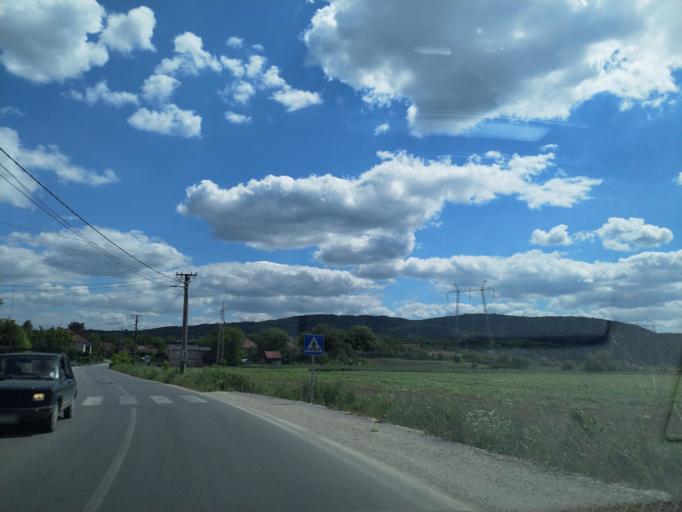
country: RS
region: Central Serbia
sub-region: Pomoravski Okrug
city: Jagodina
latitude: 43.9532
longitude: 21.2909
